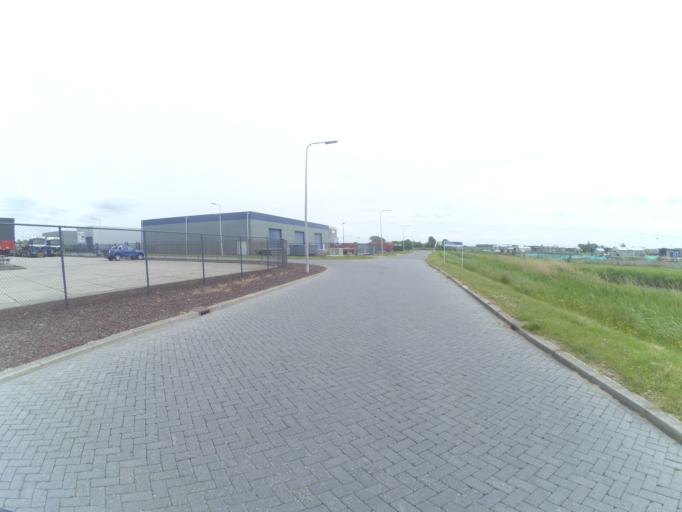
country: NL
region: South Holland
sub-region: Gemeente Spijkenisse
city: Spijkenisse
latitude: 51.8194
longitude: 4.2477
